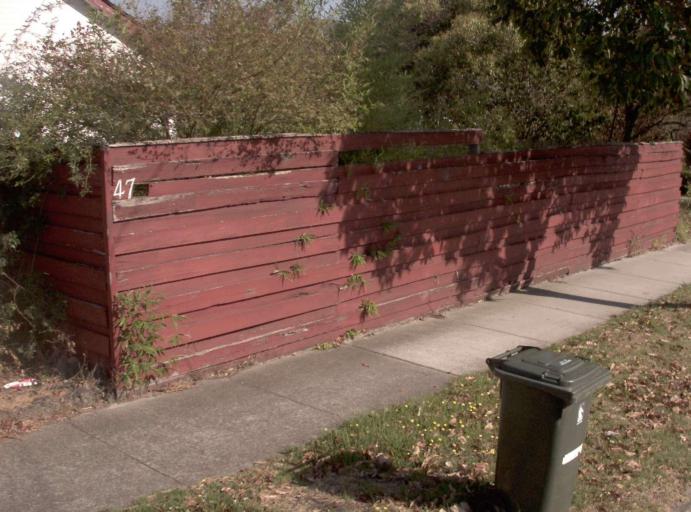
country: AU
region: Victoria
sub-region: Whitehorse
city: Burwood
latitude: -37.8523
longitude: 145.1196
